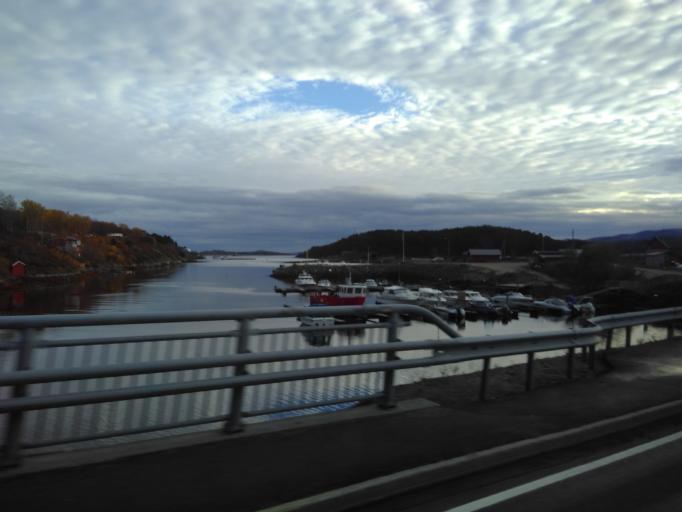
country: NO
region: Sor-Trondelag
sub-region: Hitra
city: Fillan
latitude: 63.5224
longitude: 9.1036
